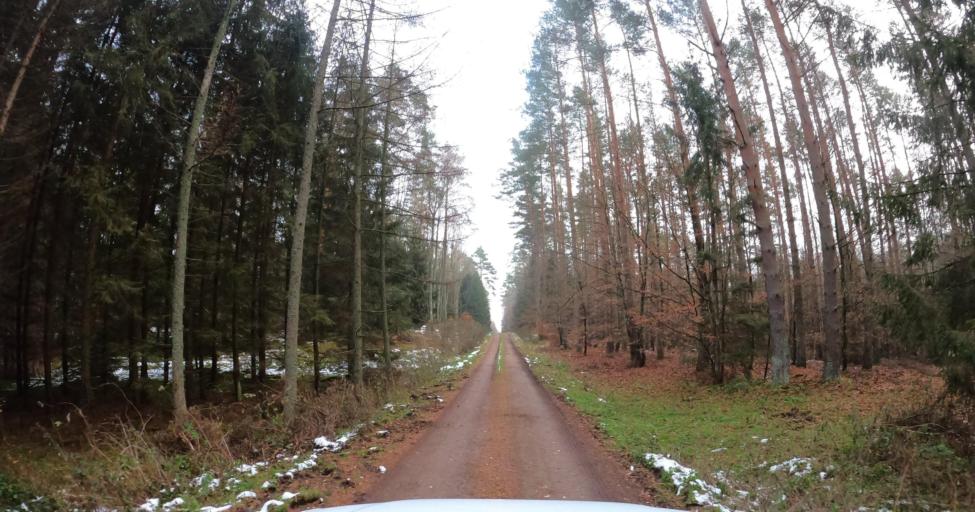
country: PL
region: West Pomeranian Voivodeship
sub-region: Powiat swidwinski
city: Rabino
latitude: 53.9066
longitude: 15.8860
